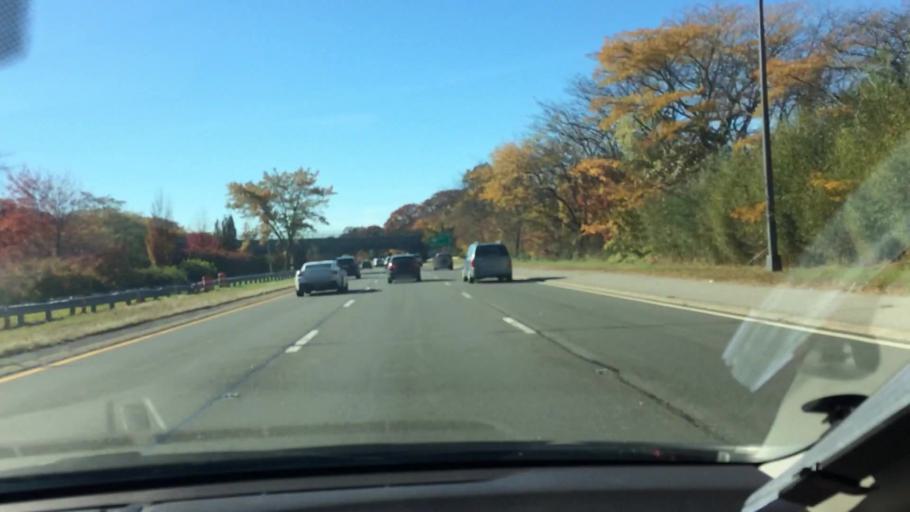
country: US
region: New York
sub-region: Suffolk County
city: North Amityville
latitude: 40.7081
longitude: -73.4219
